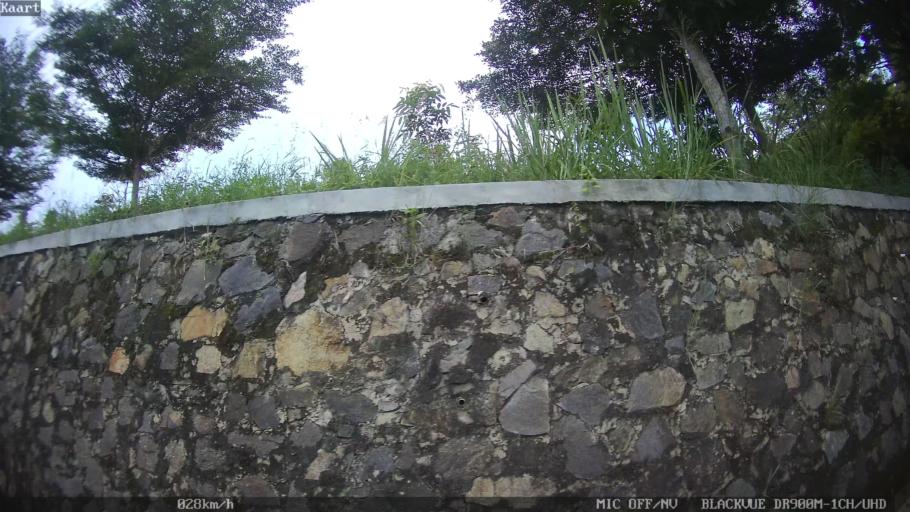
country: ID
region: Lampung
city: Kedaton
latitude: -5.3822
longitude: 105.2112
